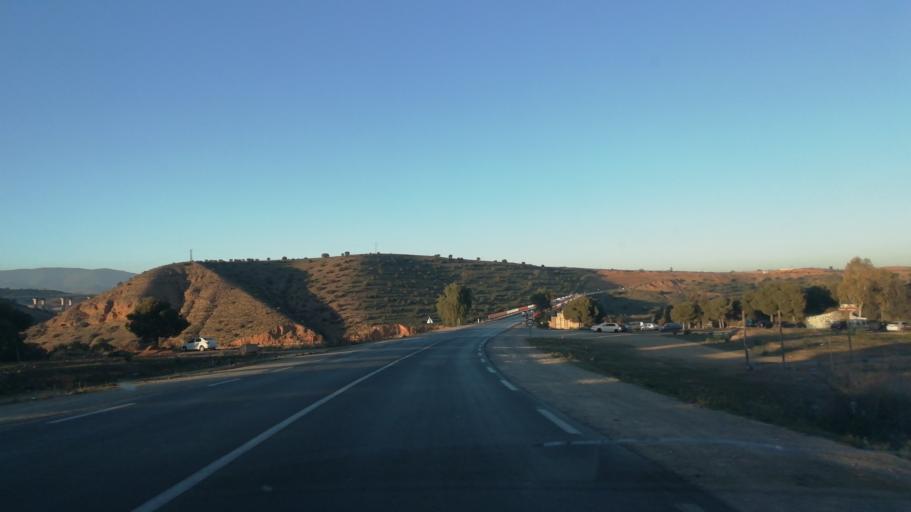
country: DZ
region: Tlemcen
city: Nedroma
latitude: 34.8835
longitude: -1.6708
